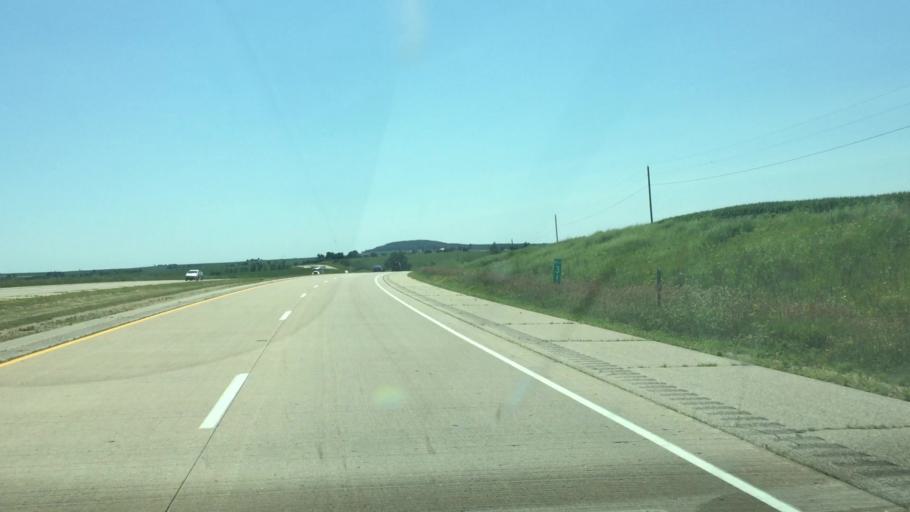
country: US
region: Wisconsin
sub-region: Iowa County
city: Mineral Point
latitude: 42.7961
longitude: -90.2821
